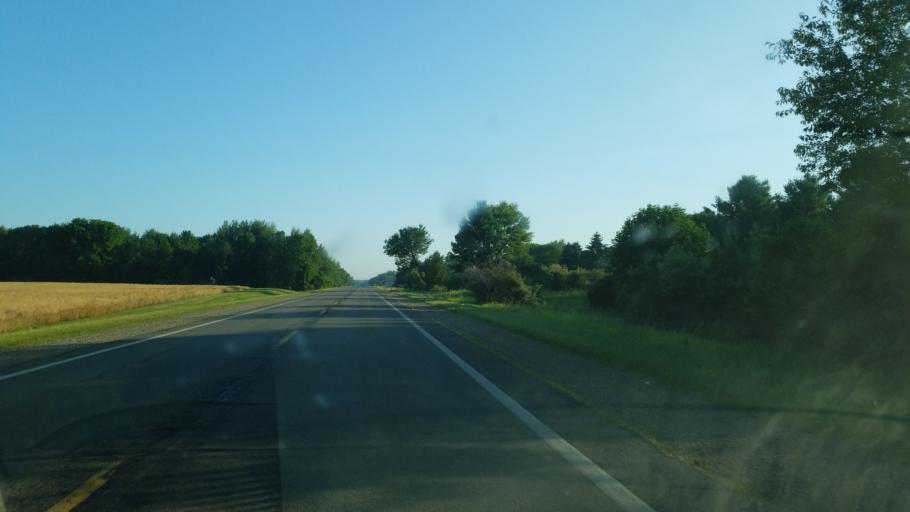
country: US
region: Michigan
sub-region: Montcalm County
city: Edmore
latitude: 43.3949
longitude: -85.0847
